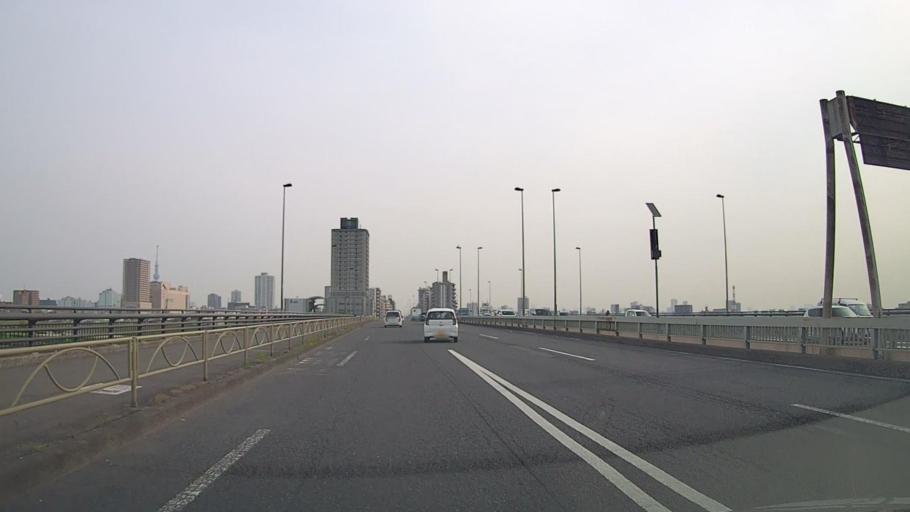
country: JP
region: Saitama
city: Soka
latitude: 35.7605
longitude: 139.8012
